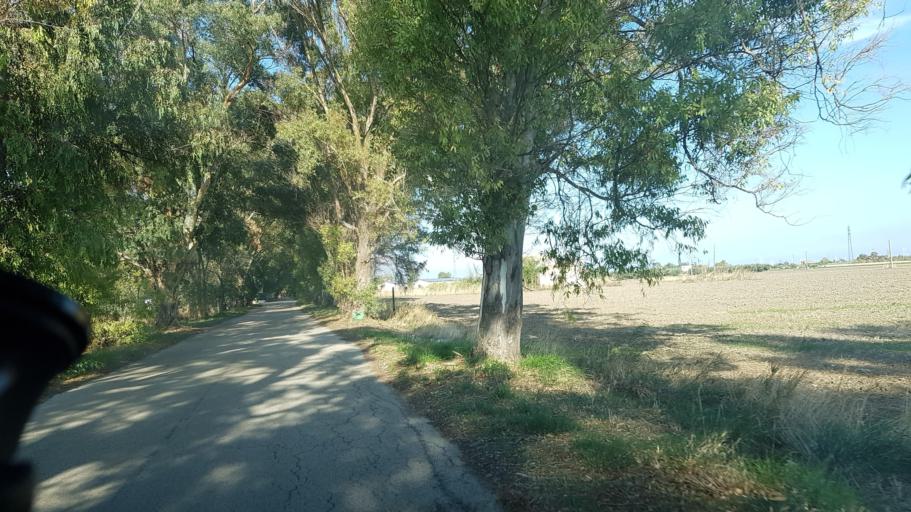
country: IT
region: Apulia
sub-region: Provincia di Foggia
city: Carapelle
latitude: 41.3918
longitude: 15.6511
